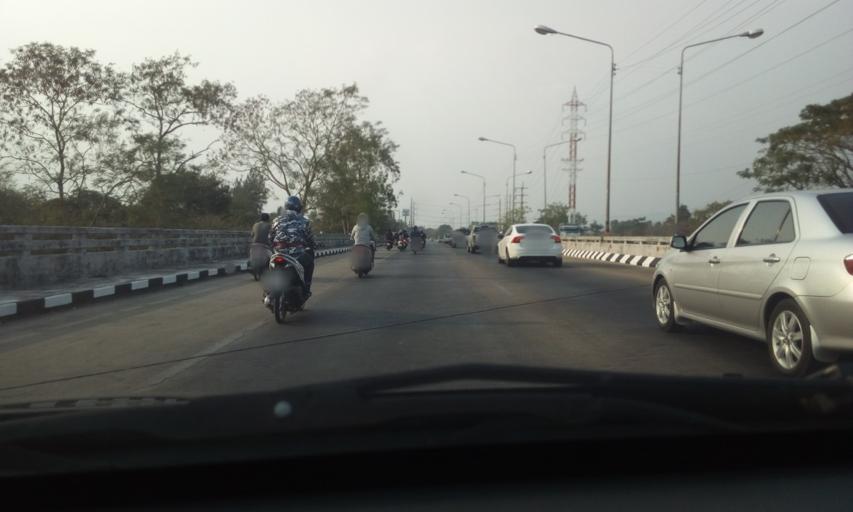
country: TH
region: Nakhon Nayok
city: Nakhon Nayok
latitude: 14.2019
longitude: 101.1906
